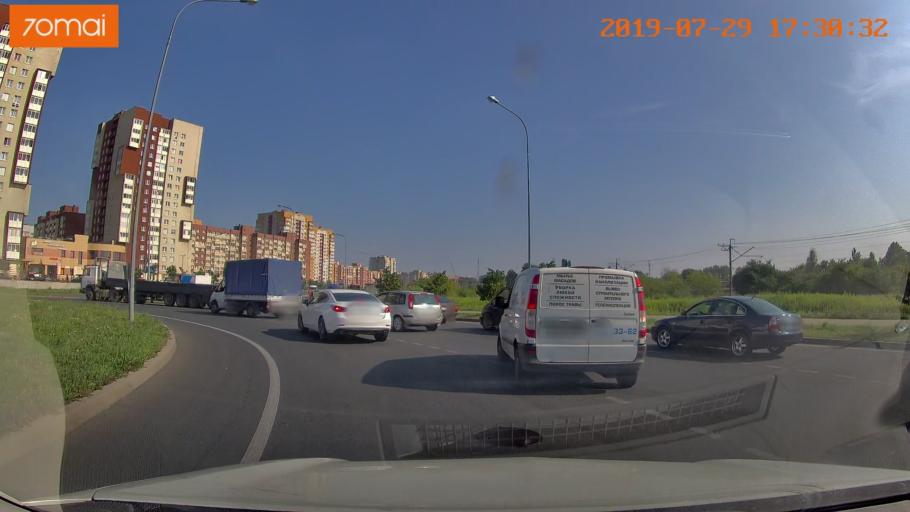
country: RU
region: Kaliningrad
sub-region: Gorod Kaliningrad
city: Kaliningrad
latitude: 54.7472
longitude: 20.4806
